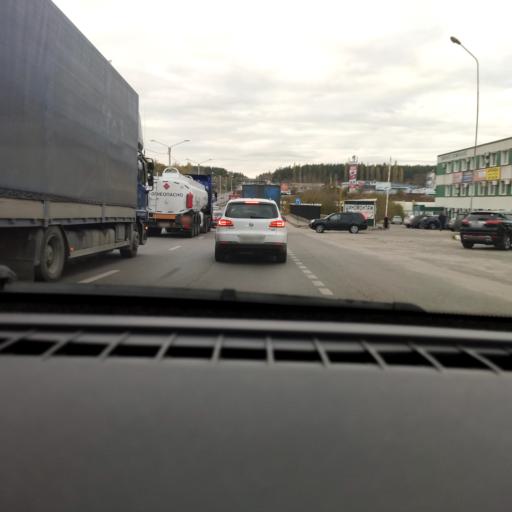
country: RU
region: Voronezj
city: Pridonskoy
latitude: 51.6692
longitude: 39.1240
